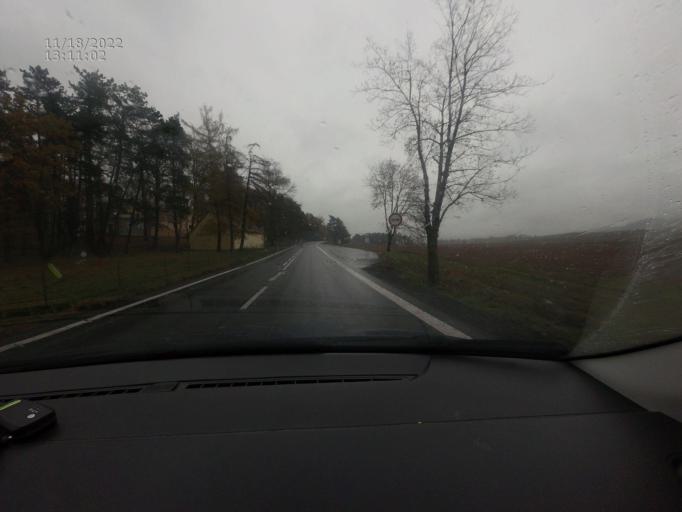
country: CZ
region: Plzensky
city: Hradek
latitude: 49.3295
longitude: 13.5758
